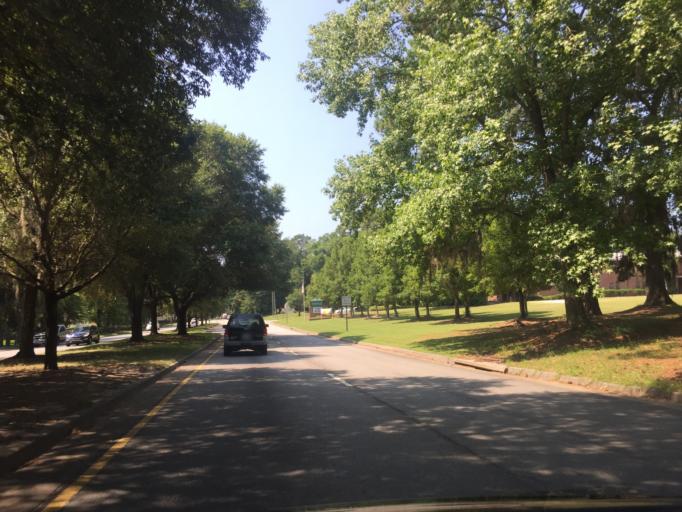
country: US
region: Georgia
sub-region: Chatham County
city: Montgomery
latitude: 31.9722
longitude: -81.1333
